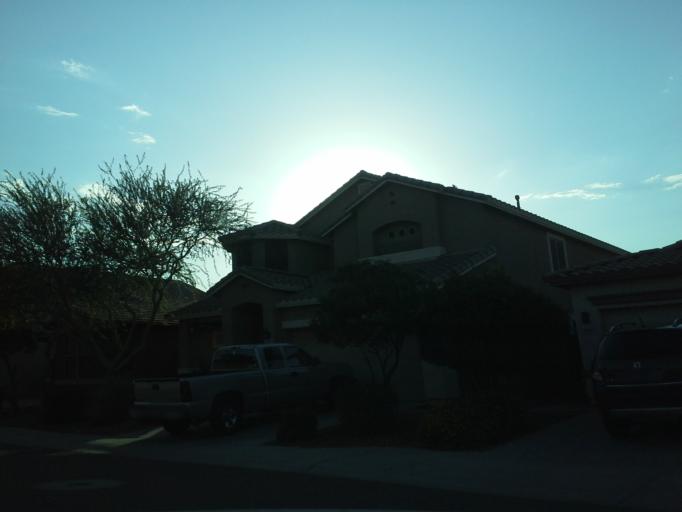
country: US
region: Arizona
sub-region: Maricopa County
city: Anthem
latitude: 33.8658
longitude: -112.1554
